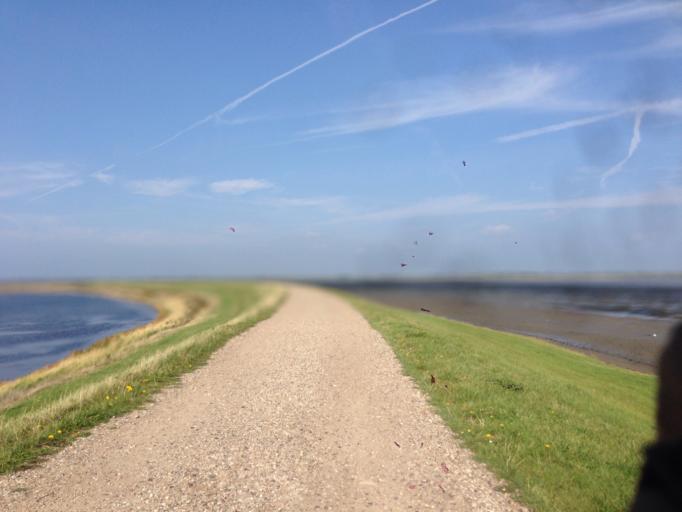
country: DE
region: Schleswig-Holstein
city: Tinnum
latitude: 54.8650
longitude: 8.3331
